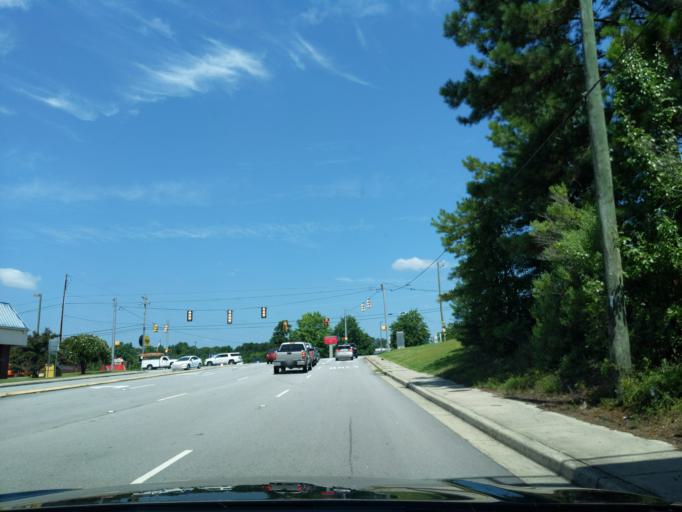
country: US
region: South Carolina
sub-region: Richland County
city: Dentsville
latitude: 34.0699
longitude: -80.9504
